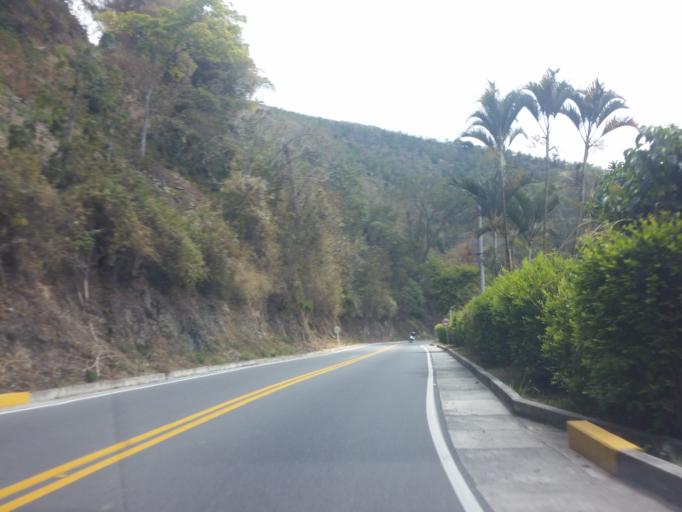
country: CO
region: Caldas
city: Villamaria
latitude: 5.0112
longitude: -75.5525
